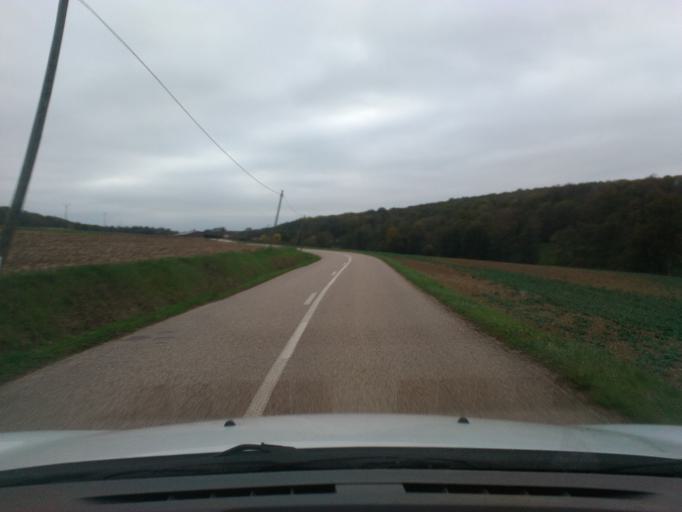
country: FR
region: Lorraine
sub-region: Departement des Vosges
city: Nomexy
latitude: 48.3103
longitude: 6.3600
